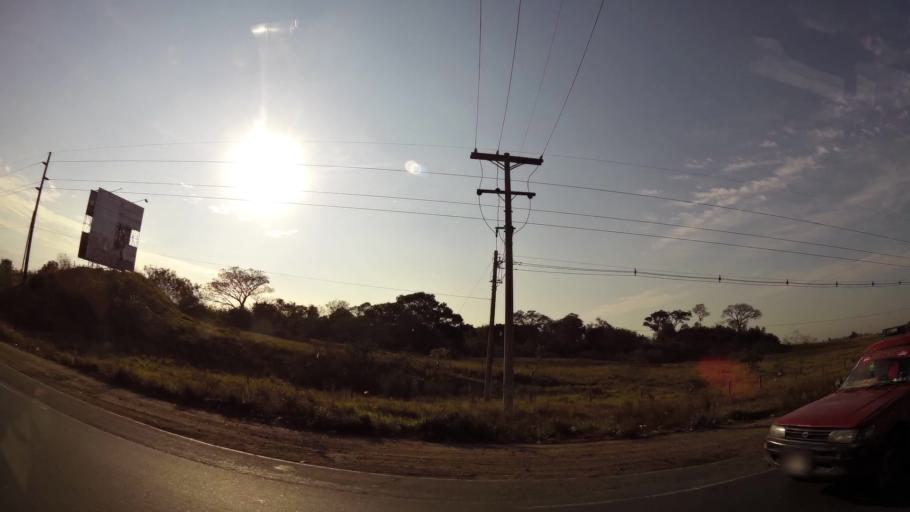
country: BO
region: Santa Cruz
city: La Belgica
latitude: -17.6616
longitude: -63.1580
